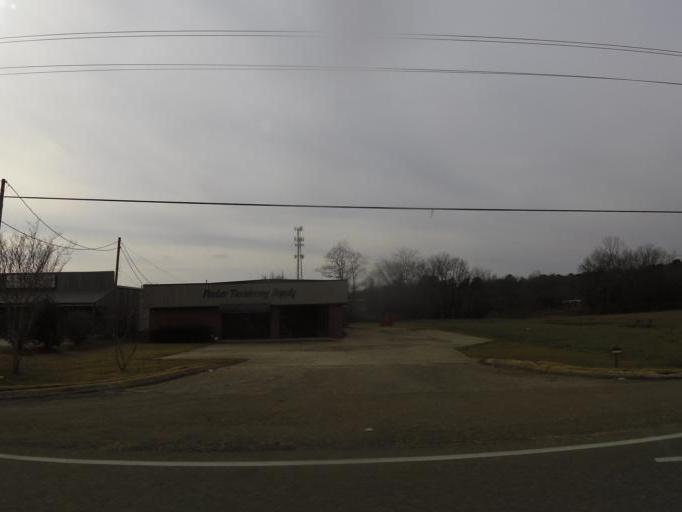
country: US
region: Alabama
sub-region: Montgomery County
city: Pike Road
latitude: 32.3041
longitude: -86.2103
